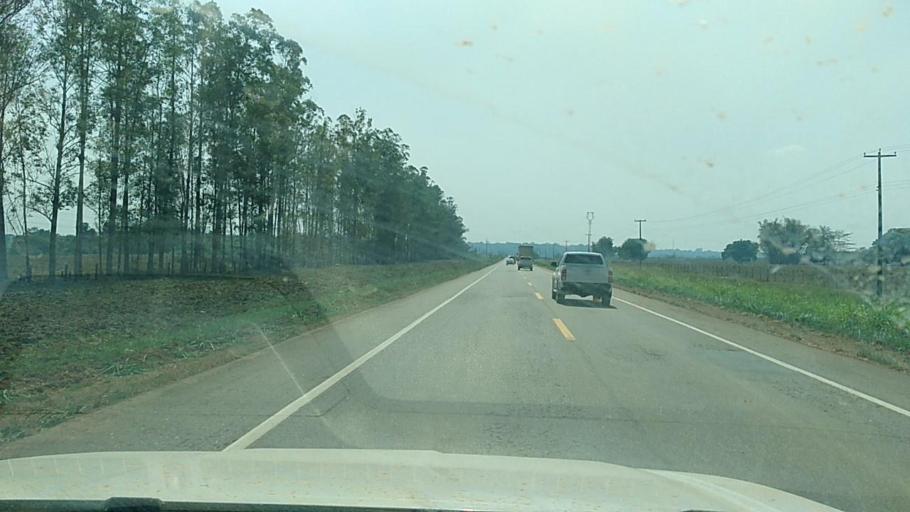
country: BR
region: Rondonia
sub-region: Porto Velho
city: Porto Velho
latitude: -8.7768
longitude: -63.5072
